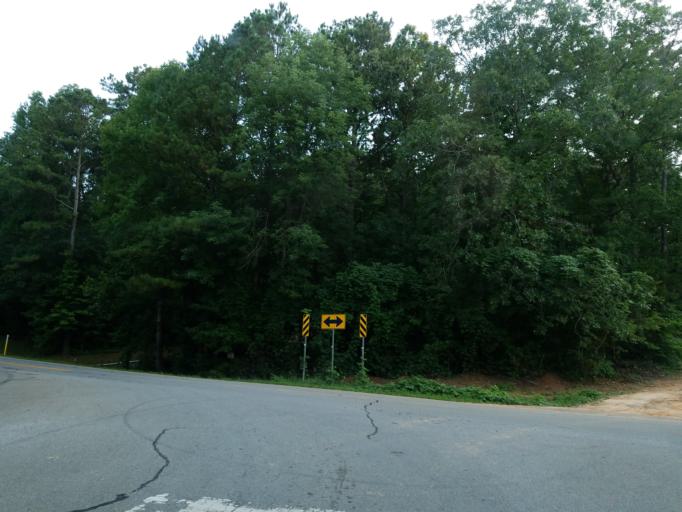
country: US
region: Georgia
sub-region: Pickens County
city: Jasper
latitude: 34.5164
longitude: -84.5020
